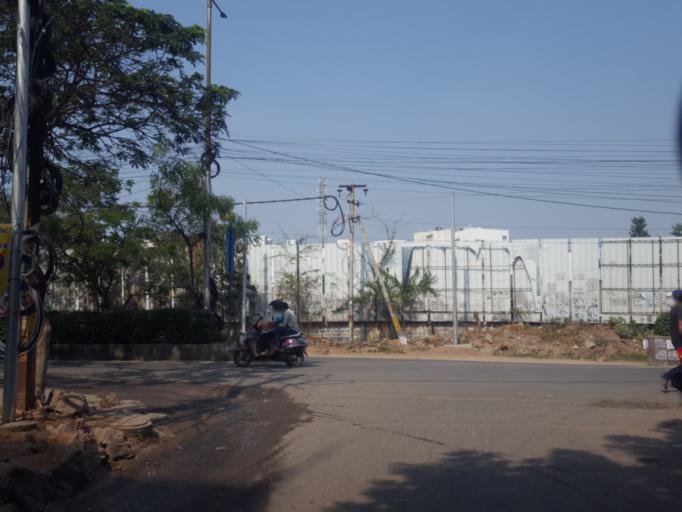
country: IN
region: Telangana
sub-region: Rangareddi
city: Kukatpalli
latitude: 17.4485
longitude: 78.3590
